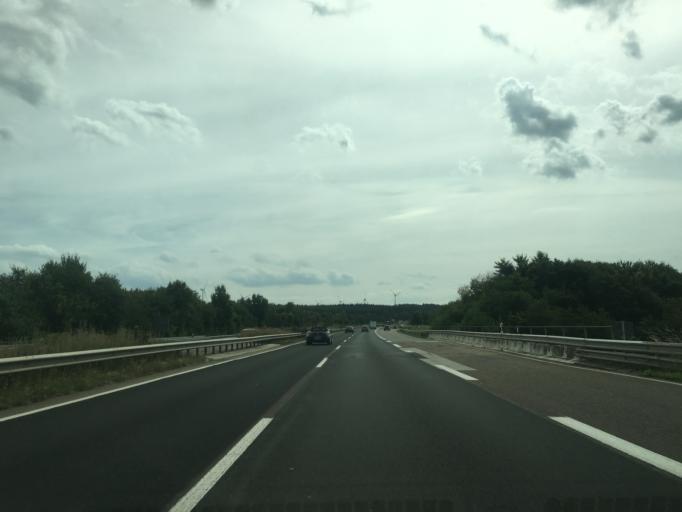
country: DE
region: Rheinland-Pfalz
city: Hungenroth
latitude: 50.1183
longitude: 7.6016
